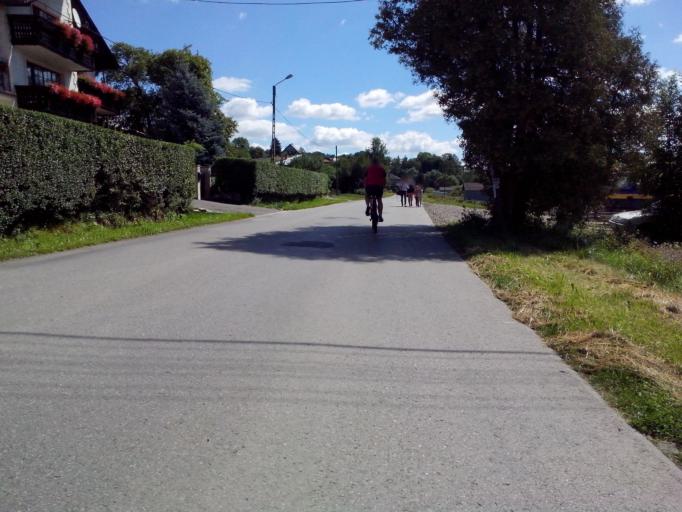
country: PL
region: Subcarpathian Voivodeship
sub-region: Powiat brzozowski
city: Domaradz
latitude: 49.7919
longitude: 21.9747
